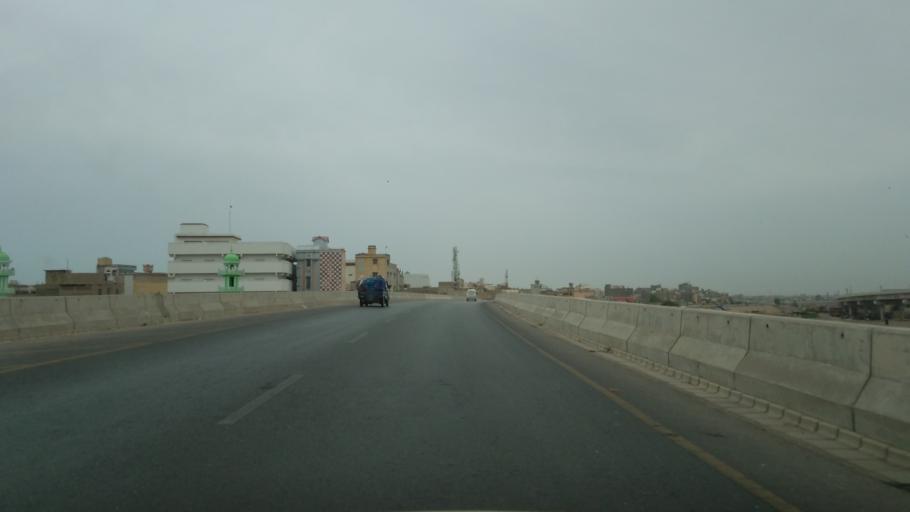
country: PK
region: Sindh
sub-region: Karachi District
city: Karachi
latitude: 24.8783
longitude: 67.0135
